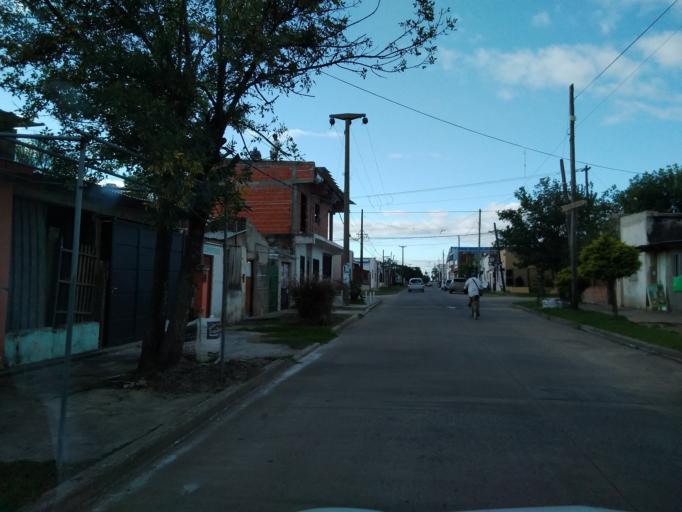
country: AR
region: Corrientes
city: Corrientes
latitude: -27.4766
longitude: -58.8059
